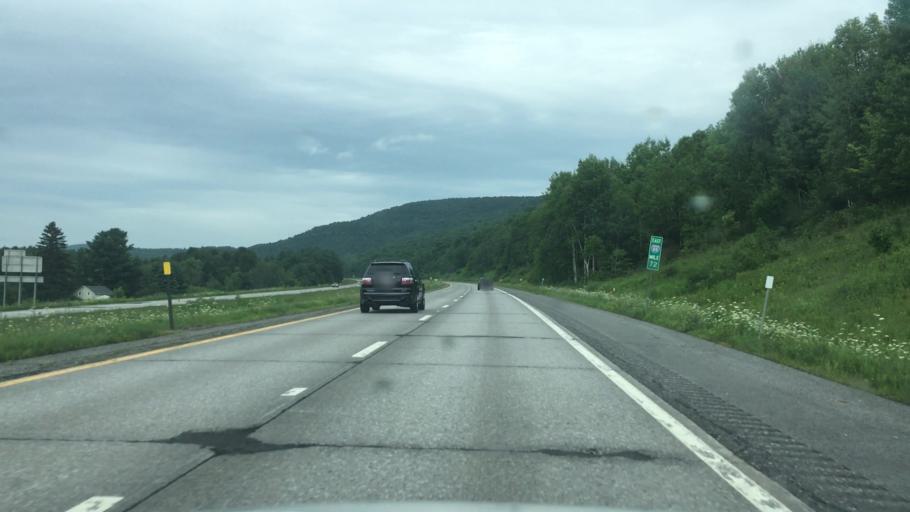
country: US
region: New York
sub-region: Otsego County
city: Worcester
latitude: 42.5549
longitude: -74.7898
